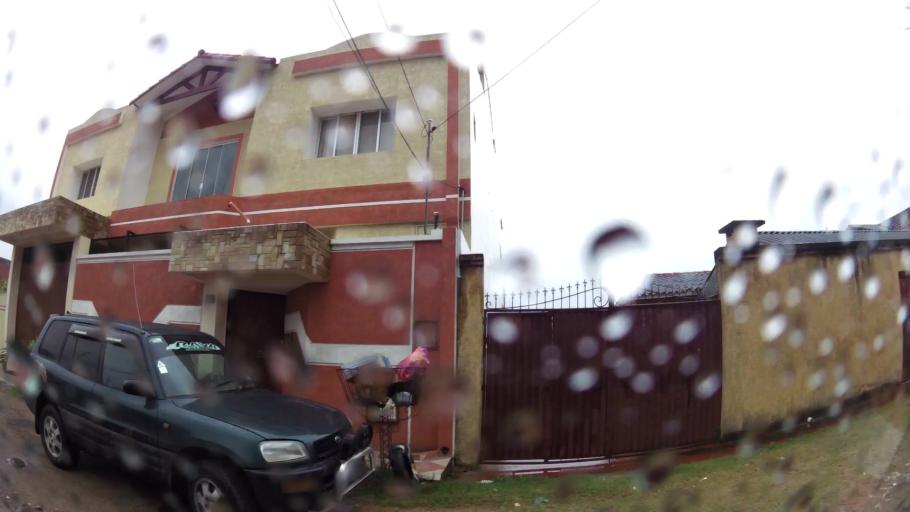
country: BO
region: Santa Cruz
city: Santa Cruz de la Sierra
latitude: -17.8132
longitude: -63.2261
